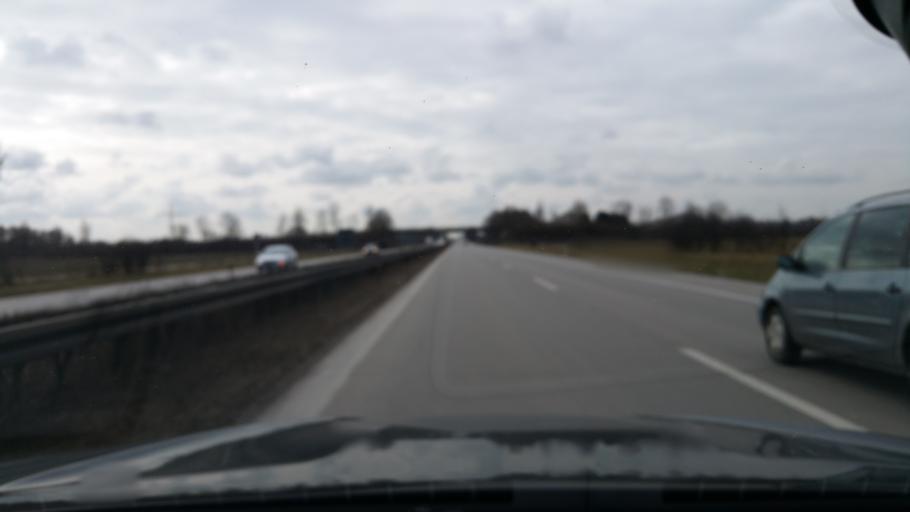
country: DE
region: Bavaria
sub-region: Upper Bavaria
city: Langenpreising
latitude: 48.4731
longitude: 11.9855
